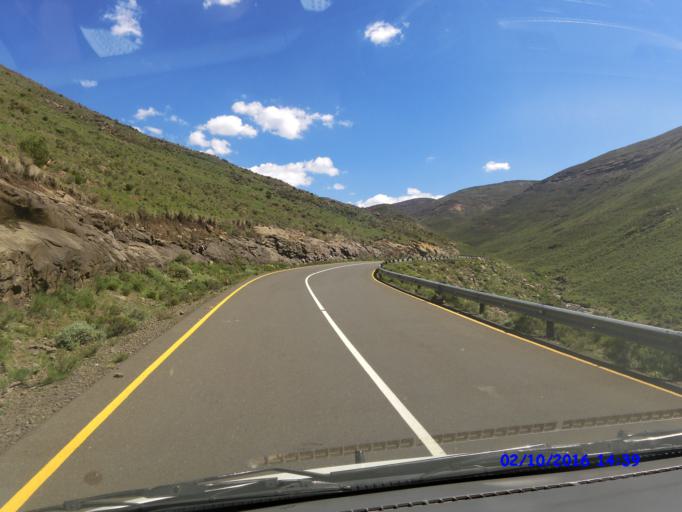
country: LS
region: Maseru
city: Nako
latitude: -29.5142
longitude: 28.0626
